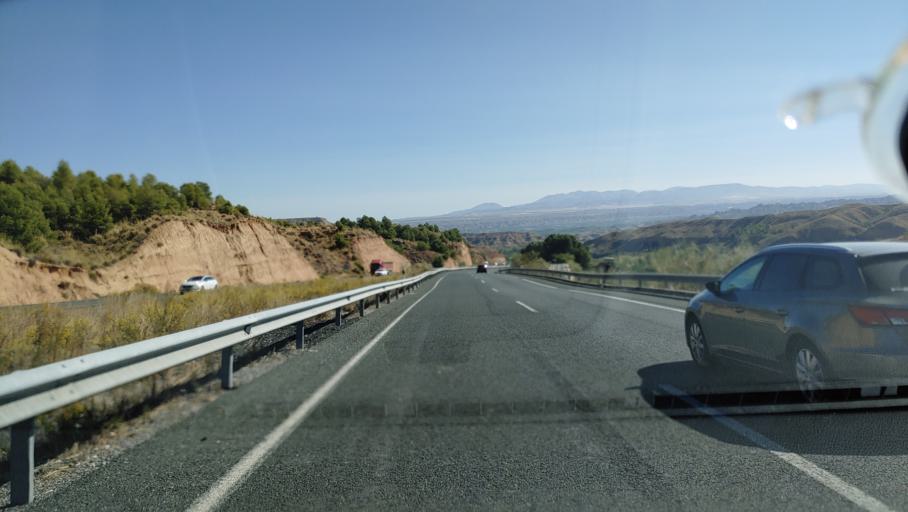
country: ES
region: Andalusia
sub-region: Provincia de Granada
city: Marchal
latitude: 37.3256
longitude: -3.2419
